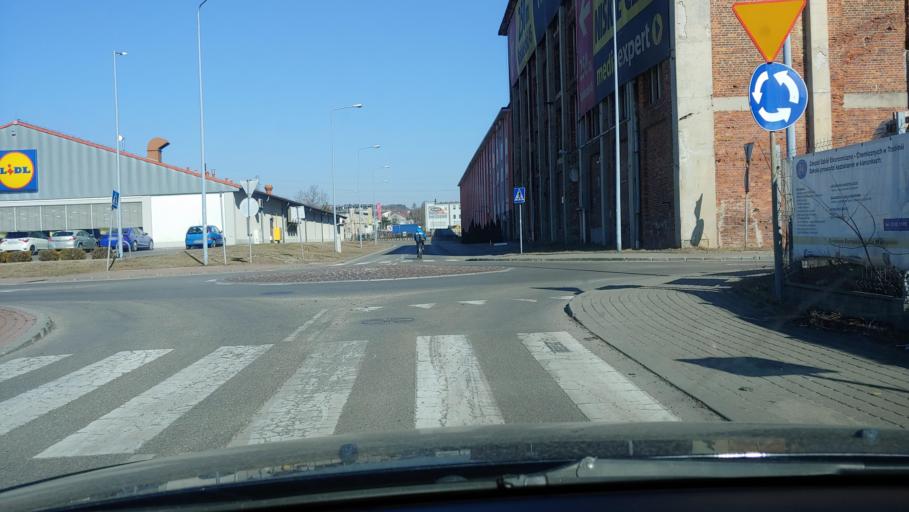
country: PL
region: Lesser Poland Voivodeship
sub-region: Powiat chrzanowski
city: Trzebinia
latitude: 50.1553
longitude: 19.4568
